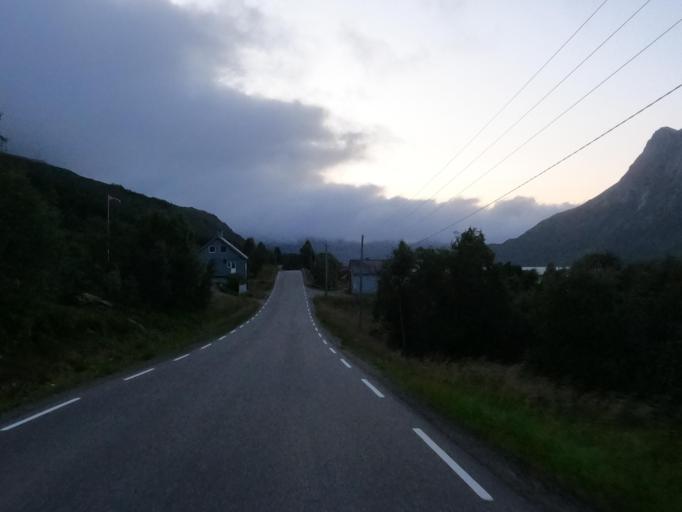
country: NO
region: Nordland
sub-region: Lodingen
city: Lodingen
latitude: 68.5822
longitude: 15.7923
